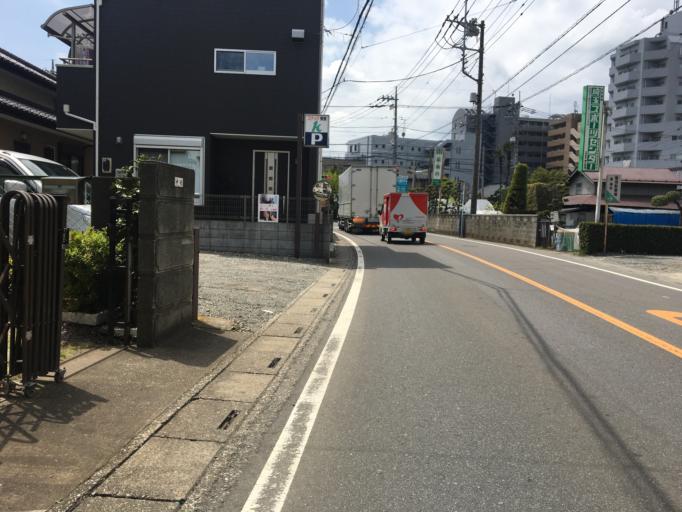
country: JP
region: Saitama
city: Shiki
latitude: 35.8394
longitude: 139.5542
